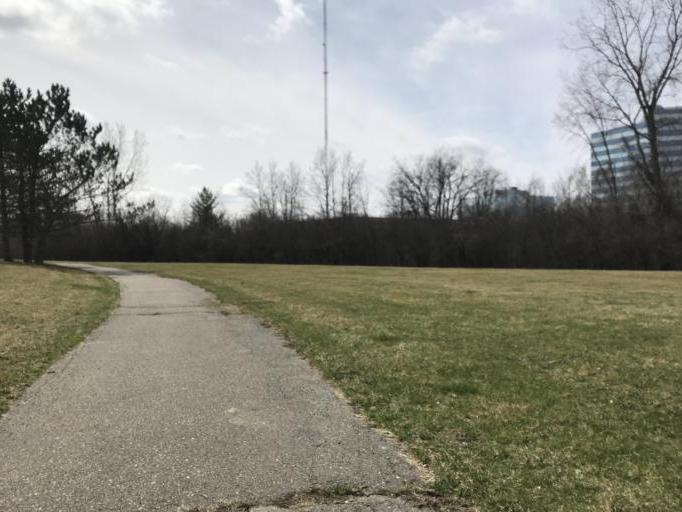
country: US
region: Michigan
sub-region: Oakland County
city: Franklin
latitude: 42.4885
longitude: -83.3094
